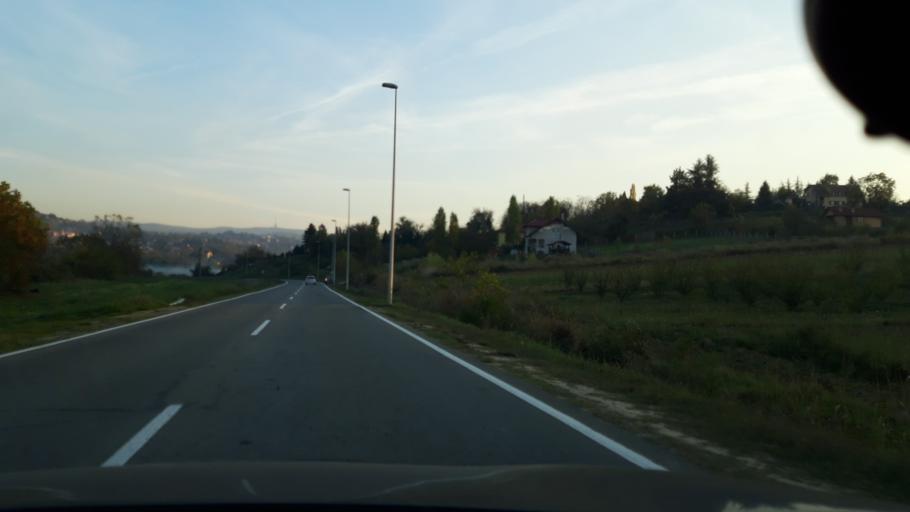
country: RS
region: Autonomna Pokrajina Vojvodina
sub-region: Juznobacki Okrug
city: Novi Sad
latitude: 45.2142
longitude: 19.8380
